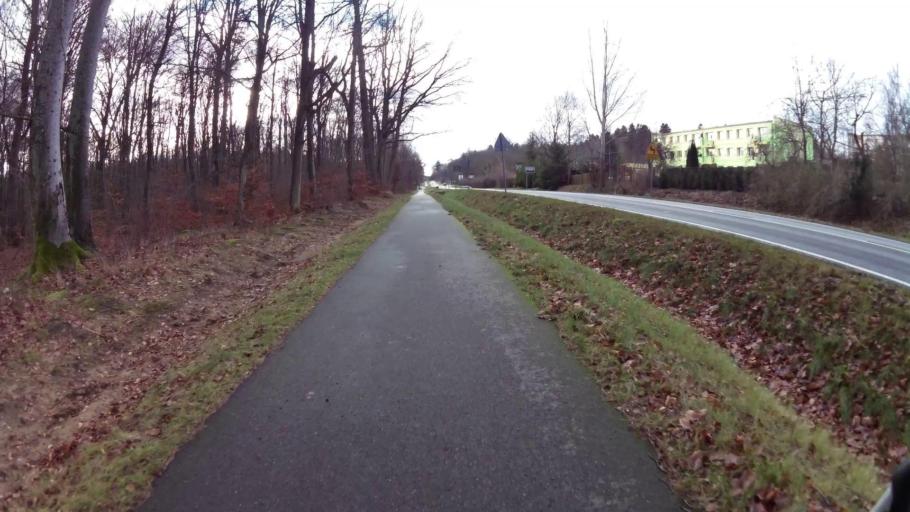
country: PL
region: West Pomeranian Voivodeship
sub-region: Koszalin
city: Koszalin
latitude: 54.1017
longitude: 16.1665
